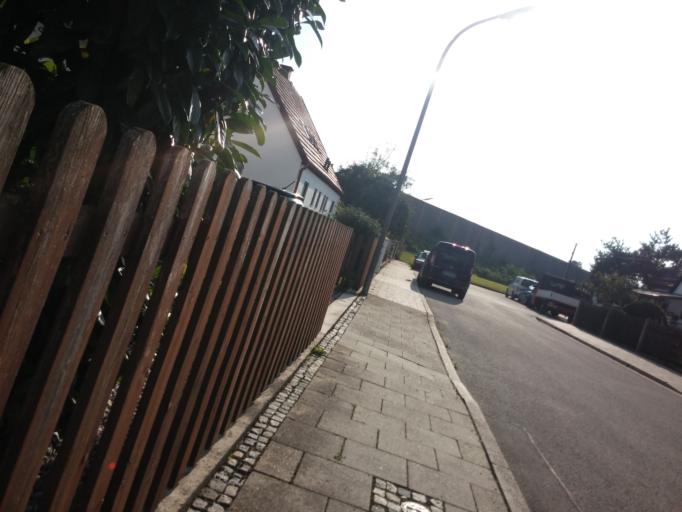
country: DE
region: Bavaria
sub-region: Upper Bavaria
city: Feldkirchen
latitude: 48.1437
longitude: 11.7375
